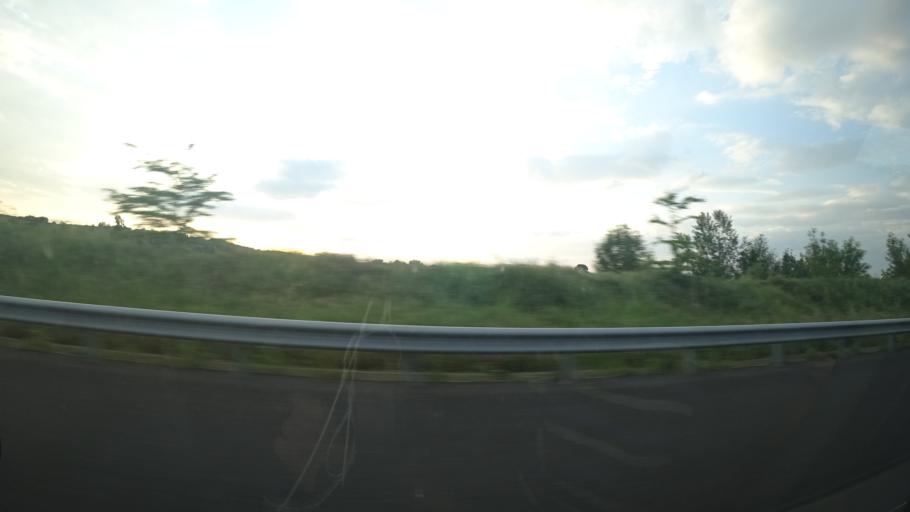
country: FR
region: Languedoc-Roussillon
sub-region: Departement de l'Herault
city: Lezignan-la-Cebe
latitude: 43.4886
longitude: 3.4428
